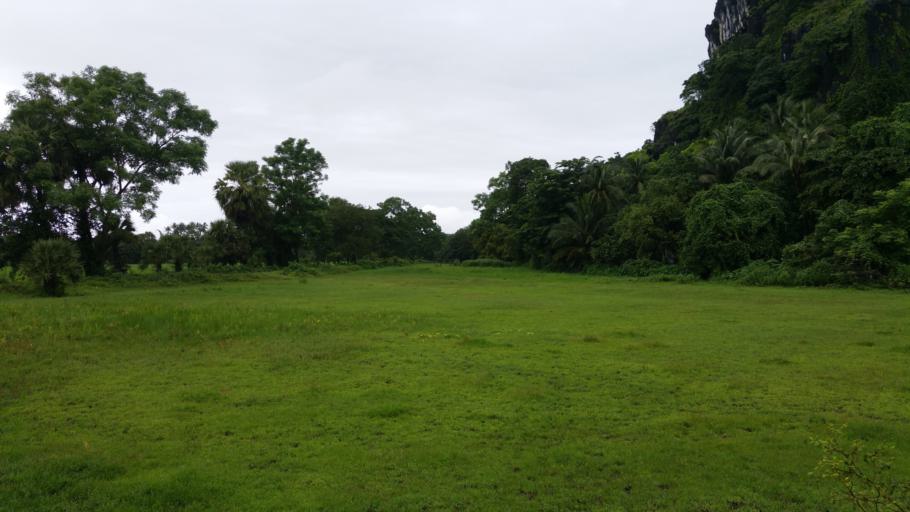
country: MM
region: Mon
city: Mudon
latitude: 16.3153
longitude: 97.7051
